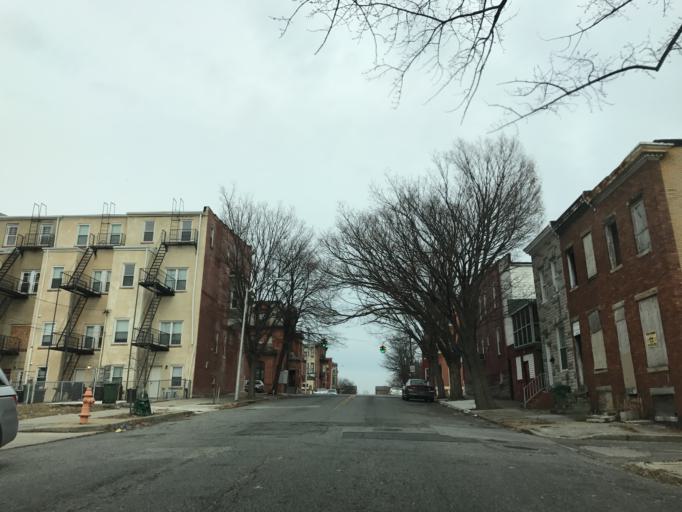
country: US
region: Maryland
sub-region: City of Baltimore
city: Baltimore
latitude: 39.3076
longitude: -76.6352
